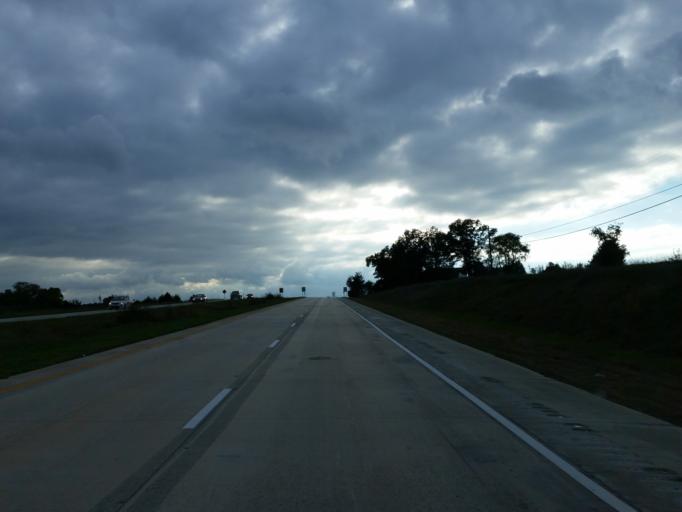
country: US
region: Georgia
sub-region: Bartow County
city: Euharlee
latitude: 34.1127
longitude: -84.8948
